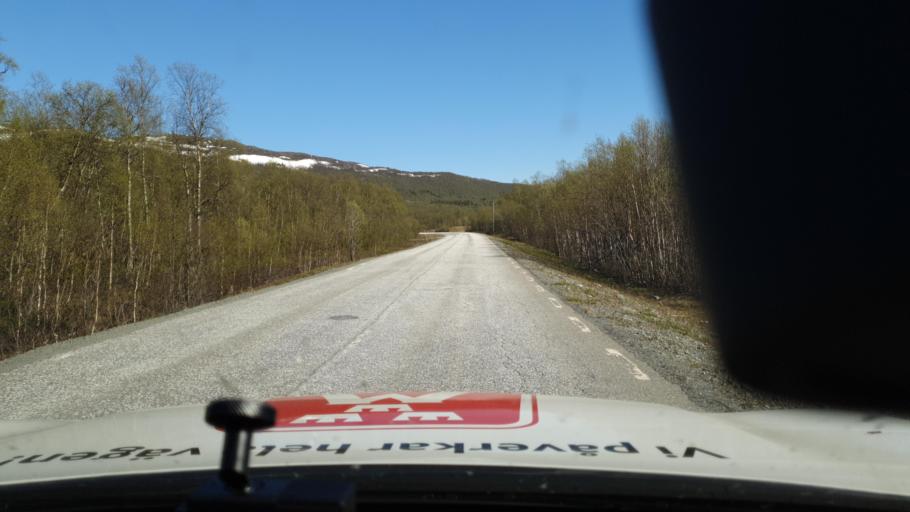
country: NO
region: Nordland
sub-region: Rana
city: Mo i Rana
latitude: 65.7830
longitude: 15.1162
